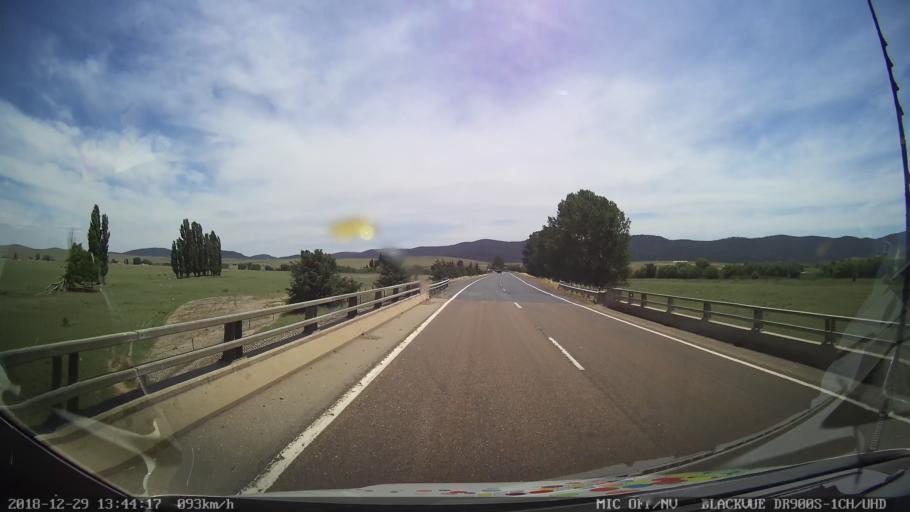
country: AU
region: New South Wales
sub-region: Cooma-Monaro
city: Cooma
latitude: -36.0828
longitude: 149.1545
